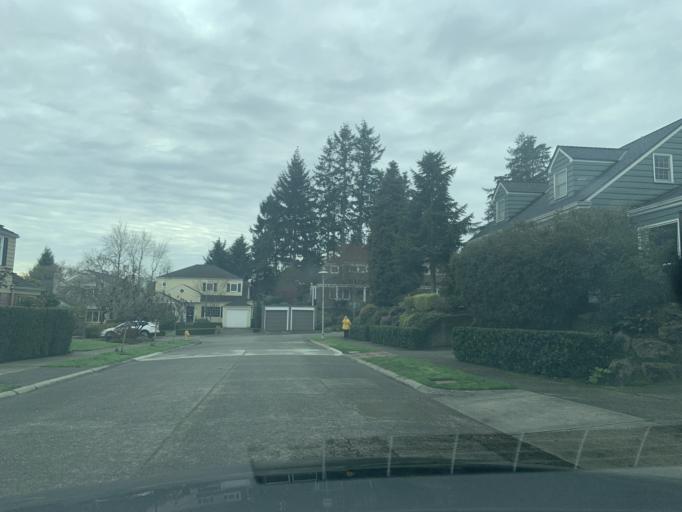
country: US
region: Washington
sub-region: King County
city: Medina
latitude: 47.6570
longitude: -122.2850
